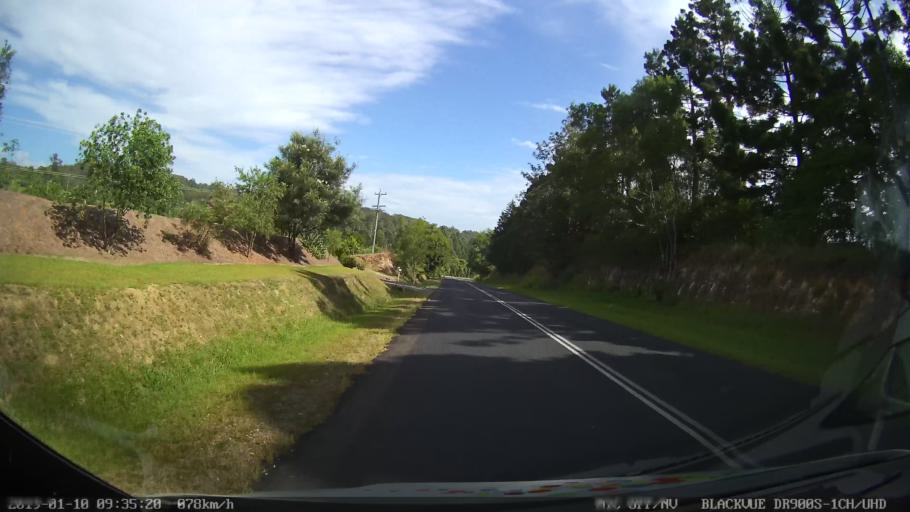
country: AU
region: New South Wales
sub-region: Coffs Harbour
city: Nana Glen
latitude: -30.2118
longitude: 153.0110
